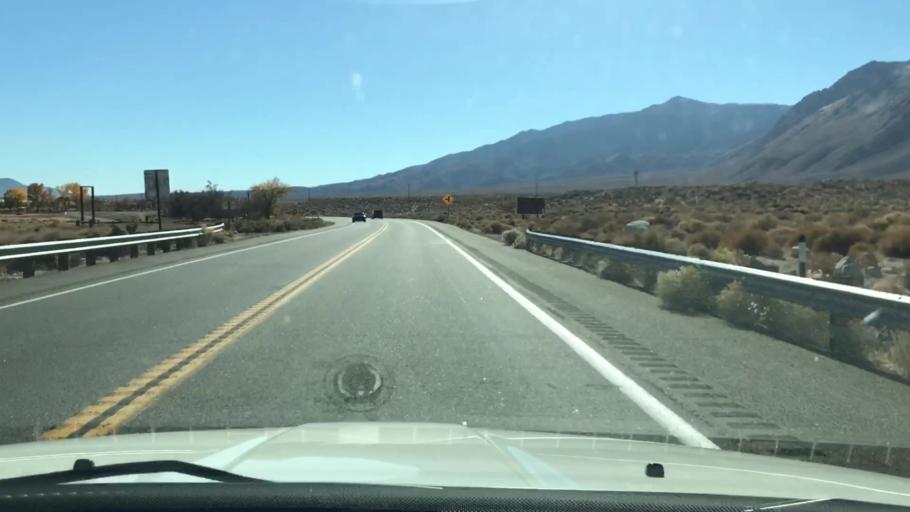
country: US
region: California
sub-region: Inyo County
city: Lone Pine
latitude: 36.3159
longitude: -118.0271
